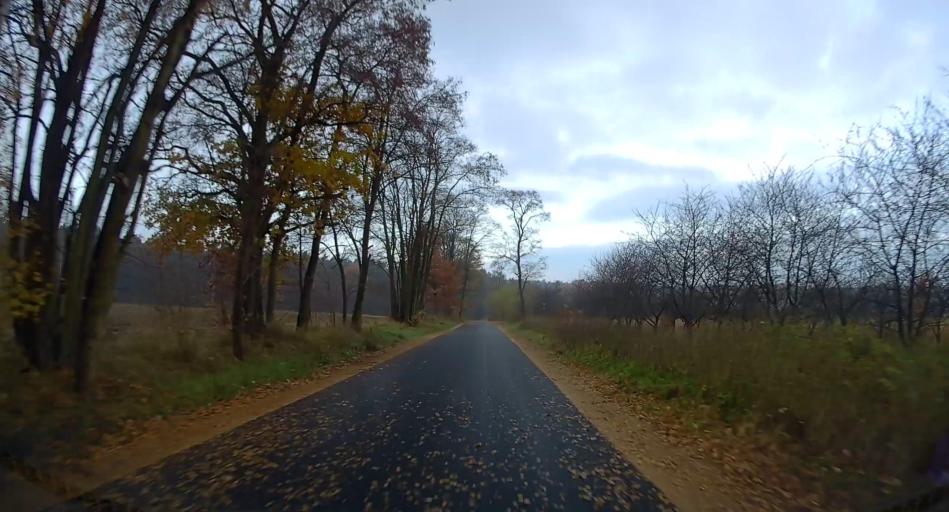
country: PL
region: Lodz Voivodeship
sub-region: Powiat skierniewicki
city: Kowiesy
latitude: 51.9288
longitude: 20.4004
